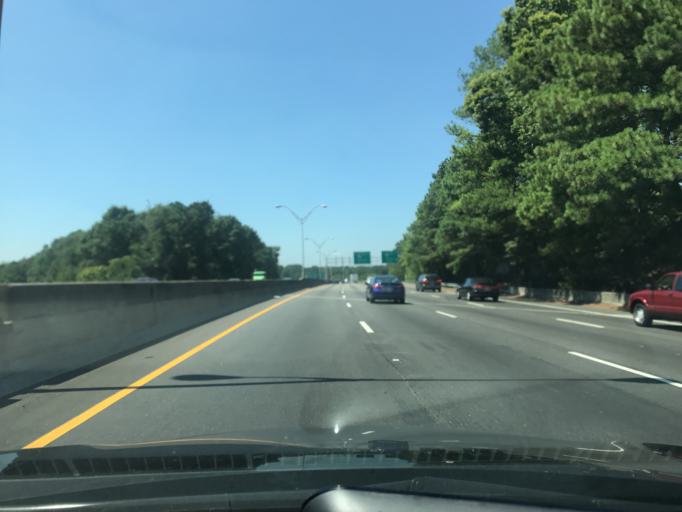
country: US
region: Georgia
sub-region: Fulton County
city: Atlanta
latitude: 33.7546
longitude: -84.4658
